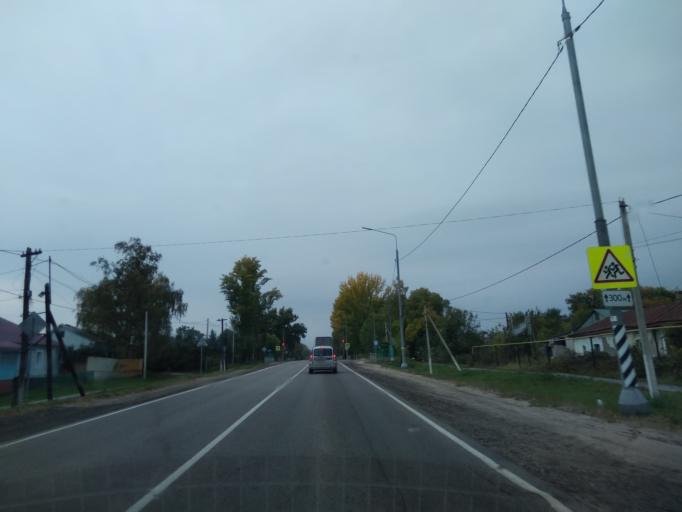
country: RU
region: Lipetsk
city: Zadonsk
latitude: 52.4141
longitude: 38.8683
